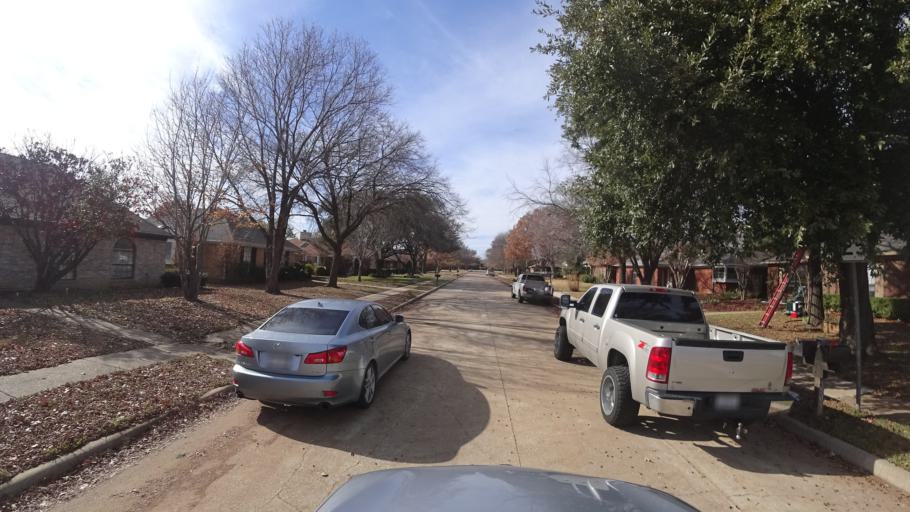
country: US
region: Texas
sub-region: Denton County
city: Highland Village
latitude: 33.0586
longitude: -97.0364
